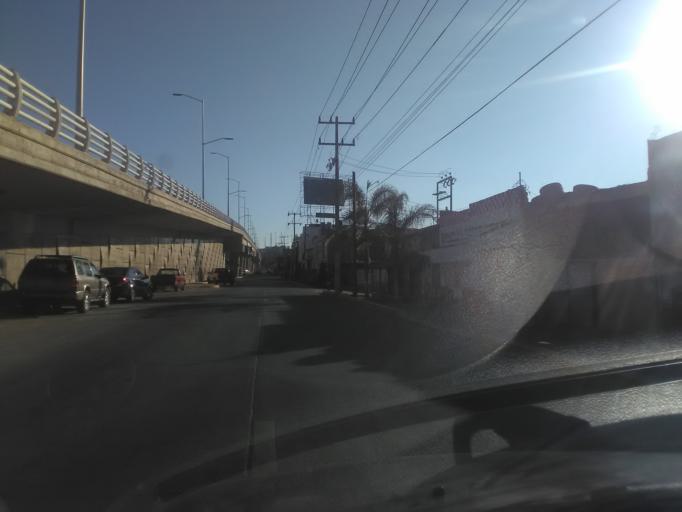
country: MX
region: Durango
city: Victoria de Durango
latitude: 24.0076
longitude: -104.6941
